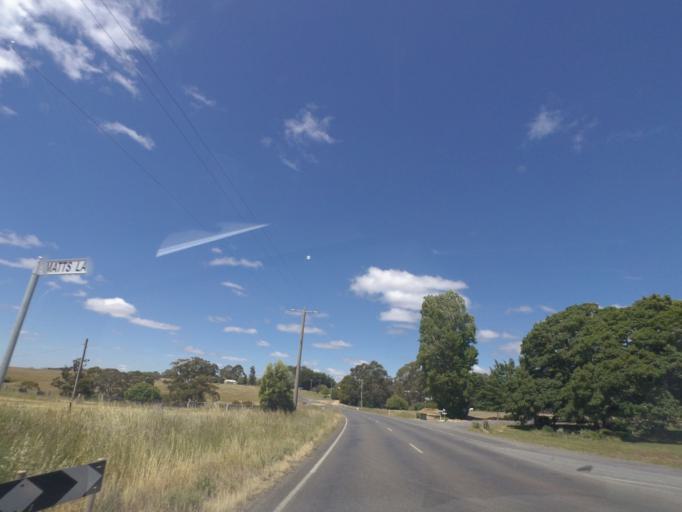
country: AU
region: Victoria
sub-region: Mount Alexander
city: Castlemaine
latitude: -37.3307
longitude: 144.1826
